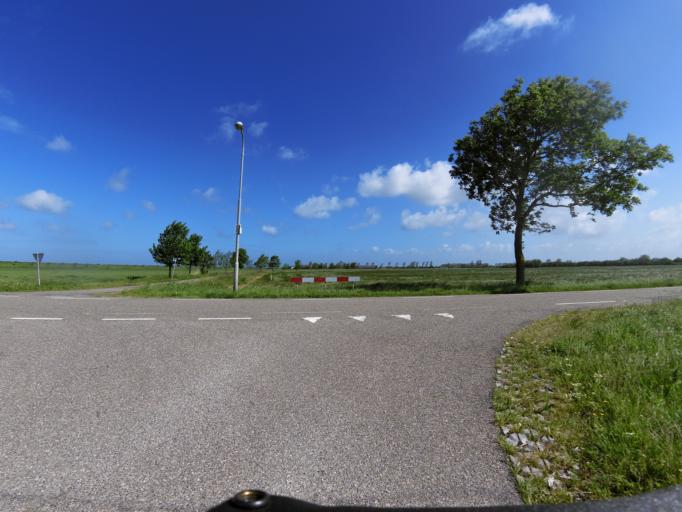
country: NL
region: Zeeland
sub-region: Schouwen-Duiveland
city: Scharendijke
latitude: 51.6933
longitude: 3.9248
